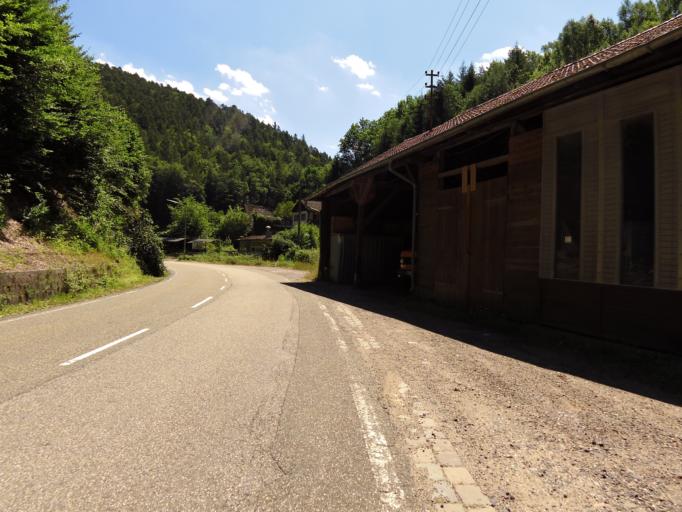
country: DE
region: Rheinland-Pfalz
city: Elmstein
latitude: 49.3569
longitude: 7.9273
